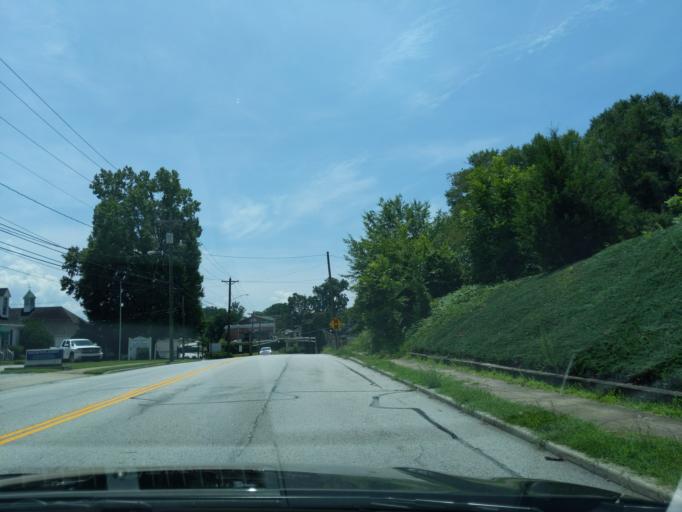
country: US
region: South Carolina
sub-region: Laurens County
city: Laurens
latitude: 34.5025
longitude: -82.0207
